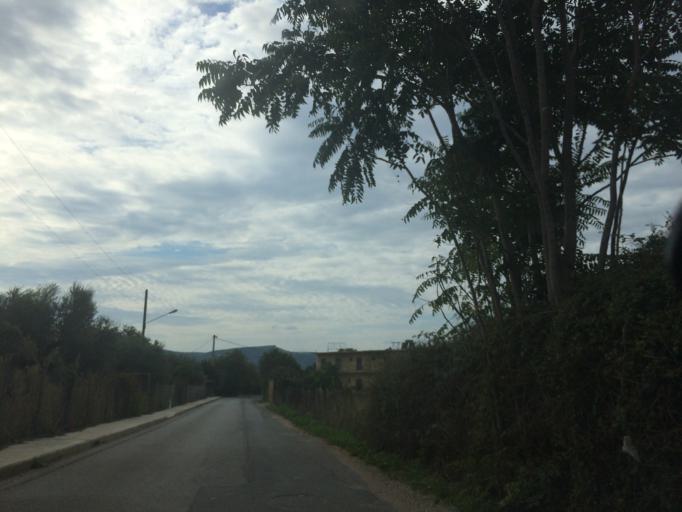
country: GR
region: Peloponnese
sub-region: Nomos Messinias
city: Pylos
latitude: 36.9542
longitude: 21.7030
